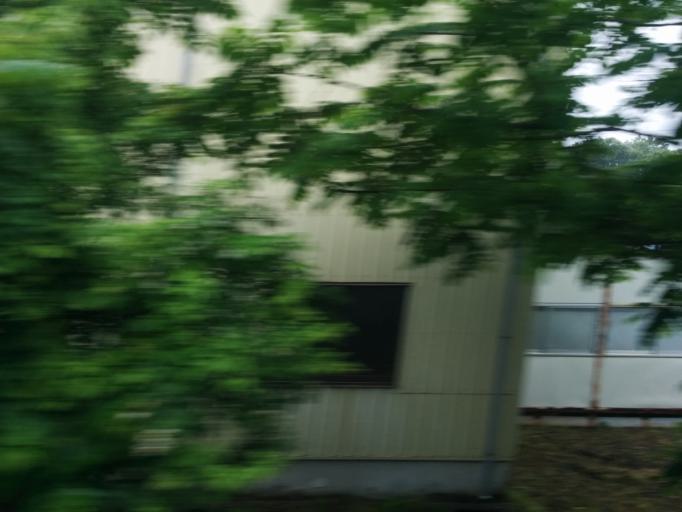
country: JP
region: Tochigi
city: Kanuma
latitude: 36.5507
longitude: 139.8013
